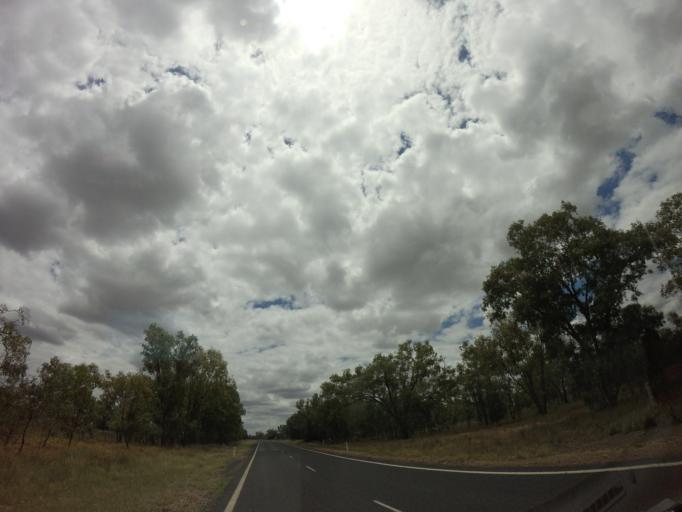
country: AU
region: Queensland
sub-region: Goondiwindi
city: Goondiwindi
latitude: -28.4842
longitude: 150.2935
